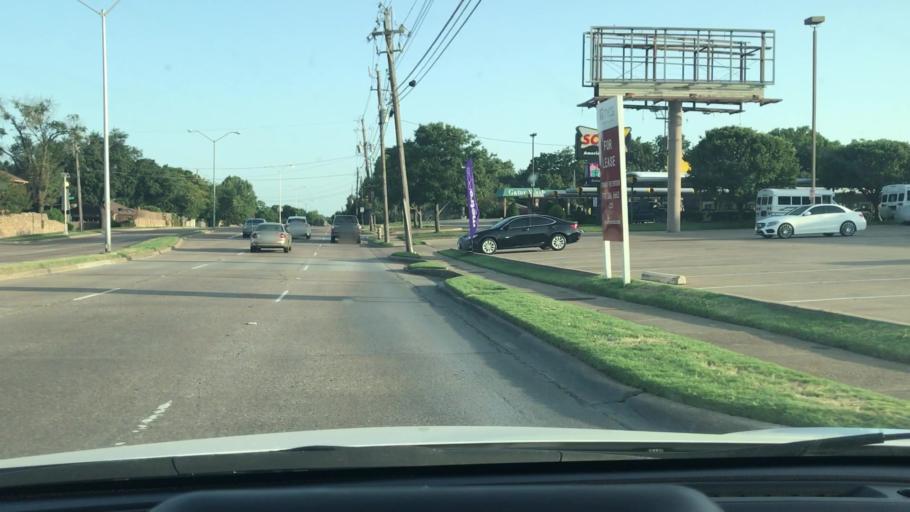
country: US
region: Texas
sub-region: Dallas County
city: Garland
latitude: 32.8785
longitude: -96.7005
